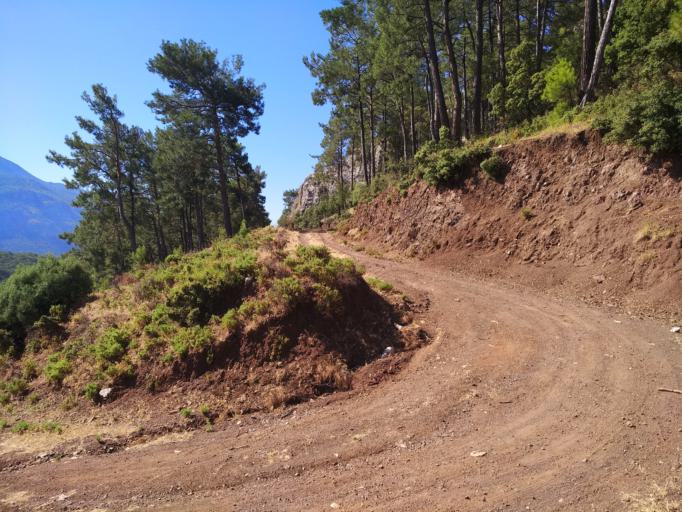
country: TR
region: Mugla
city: OEluedeniz
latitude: 36.5706
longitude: 29.1186
